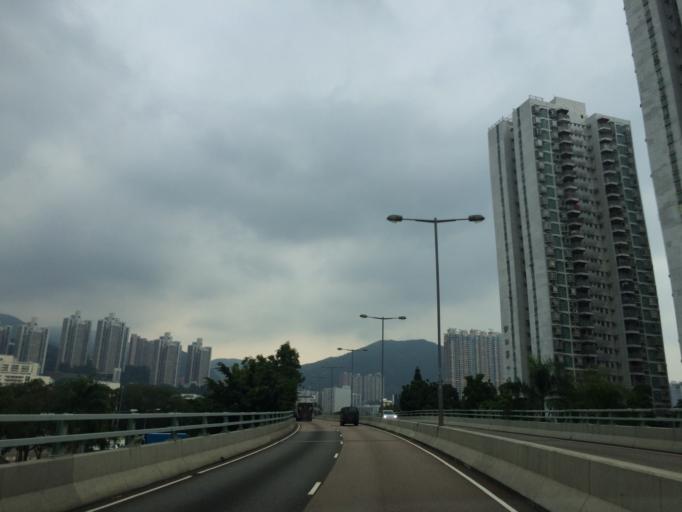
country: HK
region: Sha Tin
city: Sha Tin
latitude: 22.3863
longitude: 114.2014
